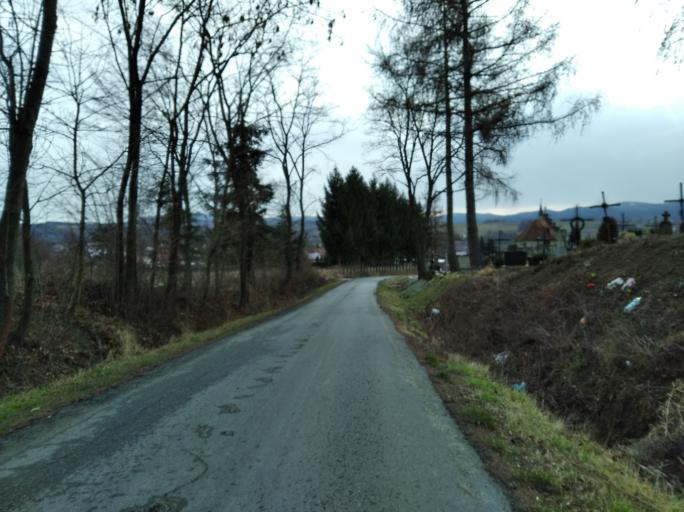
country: PL
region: Subcarpathian Voivodeship
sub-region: Powiat strzyzowski
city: Wysoka Strzyzowska
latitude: 49.8801
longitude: 21.7236
